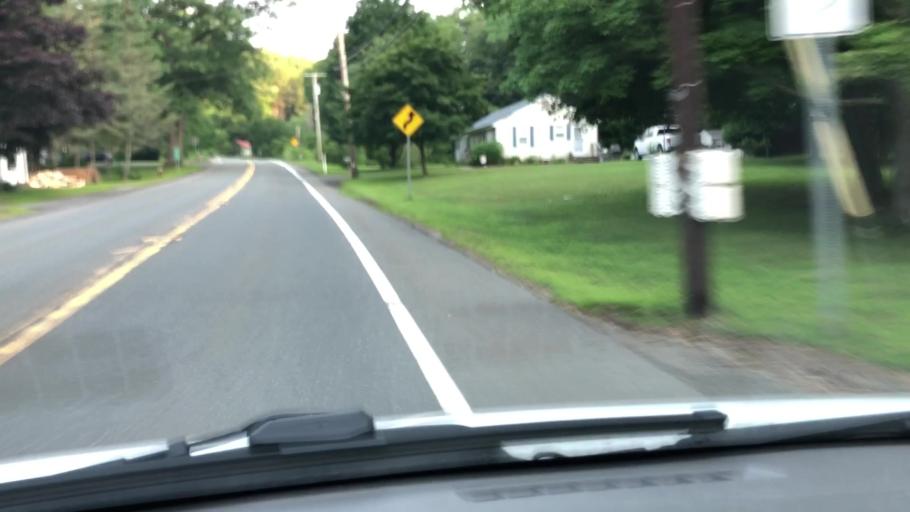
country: US
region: Massachusetts
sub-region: Hampshire County
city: Williamsburg
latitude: 42.3949
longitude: -72.7377
